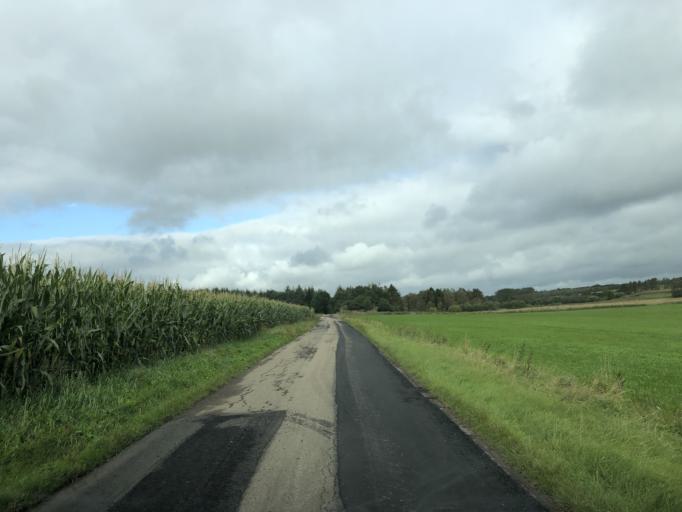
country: DK
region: Central Jutland
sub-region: Holstebro Kommune
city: Ulfborg
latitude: 56.3005
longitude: 8.4404
